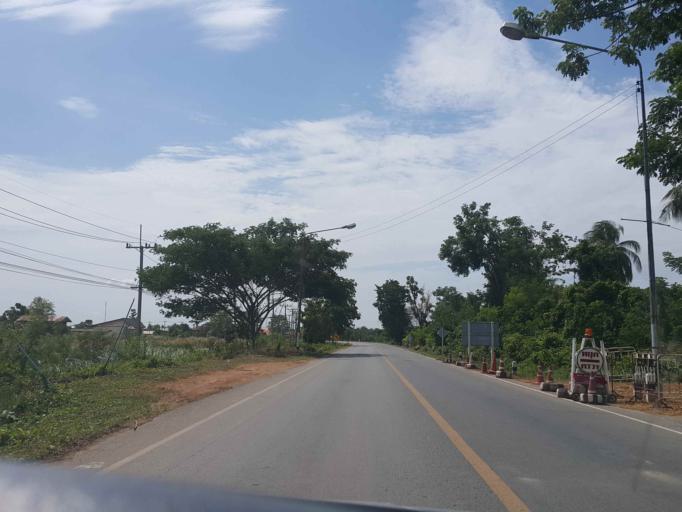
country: TH
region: Sukhothai
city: Thung Saliam
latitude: 17.3286
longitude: 99.5046
